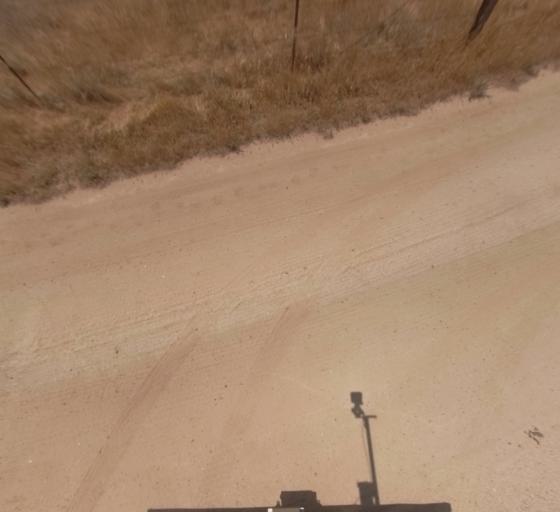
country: US
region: California
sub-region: Madera County
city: Madera Acres
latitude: 37.1230
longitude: -120.0818
